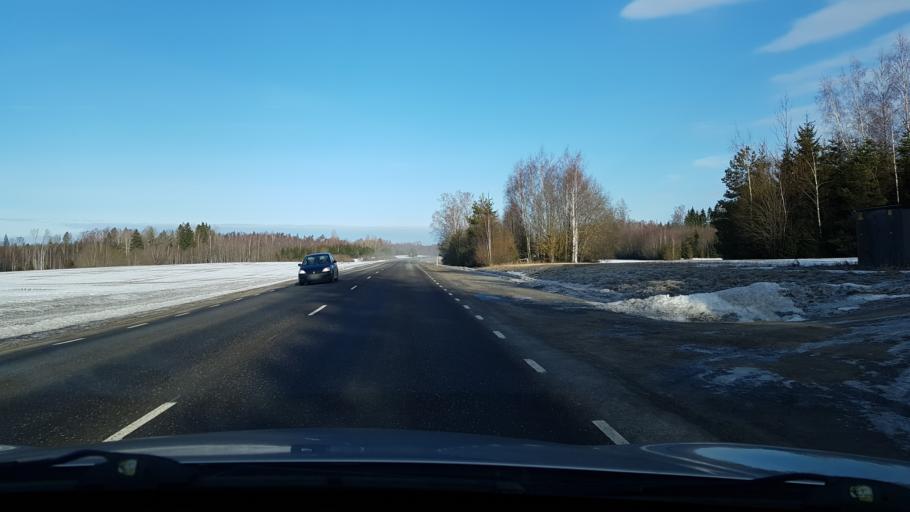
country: EE
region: Viljandimaa
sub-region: Viljandi linn
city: Viljandi
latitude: 58.4280
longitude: 25.5967
